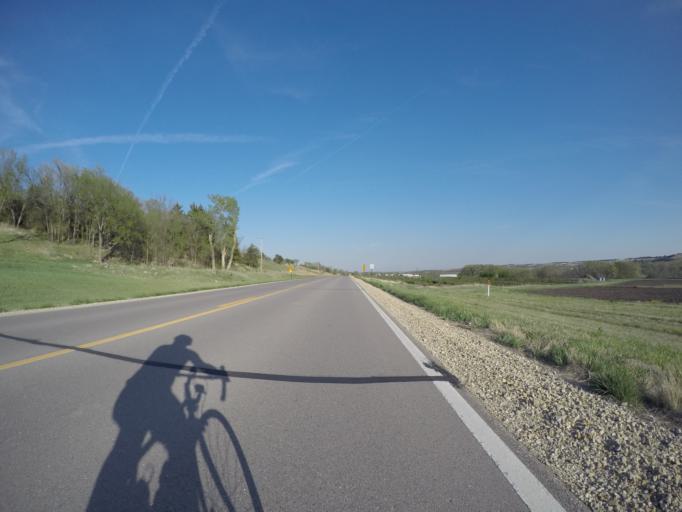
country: US
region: Kansas
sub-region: Riley County
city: Manhattan
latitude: 39.1978
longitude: -96.6514
